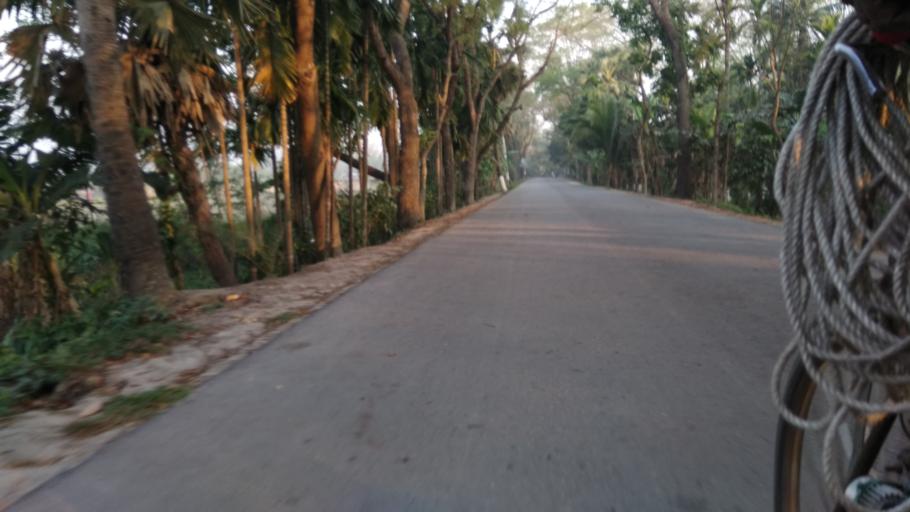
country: BD
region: Barisal
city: Mehendiganj
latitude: 22.9193
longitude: 90.4096
